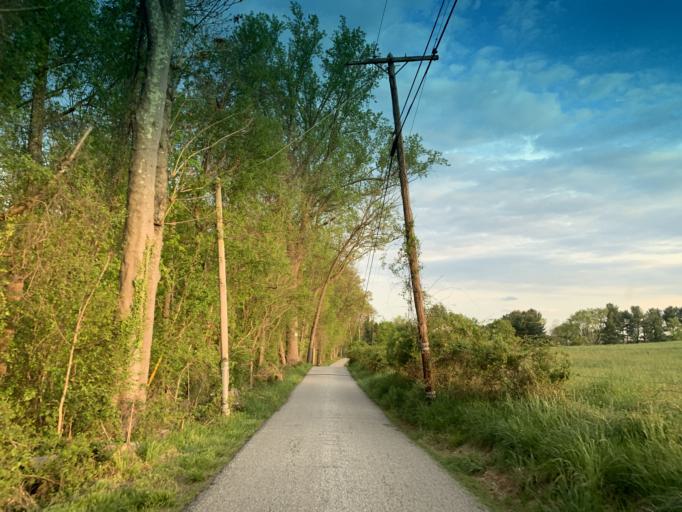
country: US
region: Maryland
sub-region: Harford County
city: Bel Air South
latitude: 39.4948
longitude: -76.3496
